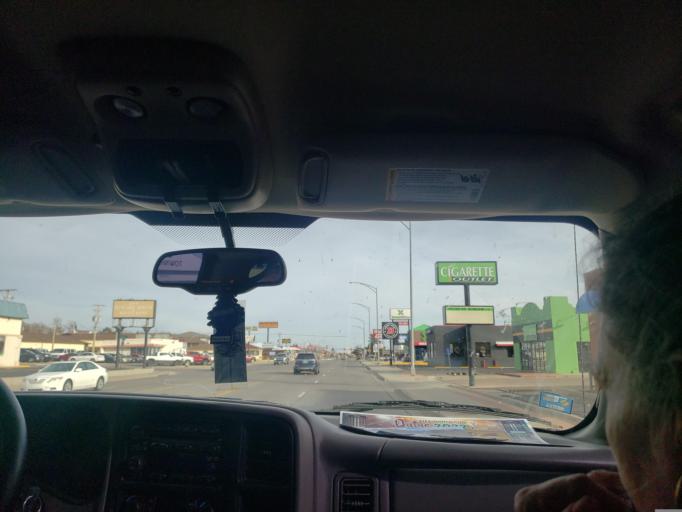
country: US
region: Kansas
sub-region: Ford County
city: Dodge City
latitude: 37.7538
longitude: -100.0361
